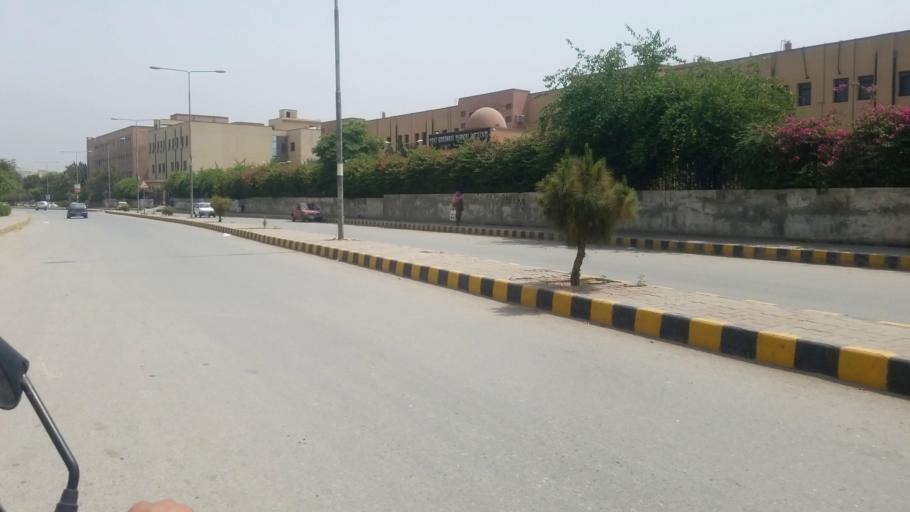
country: PK
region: Khyber Pakhtunkhwa
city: Peshawar
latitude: 33.9940
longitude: 71.4467
